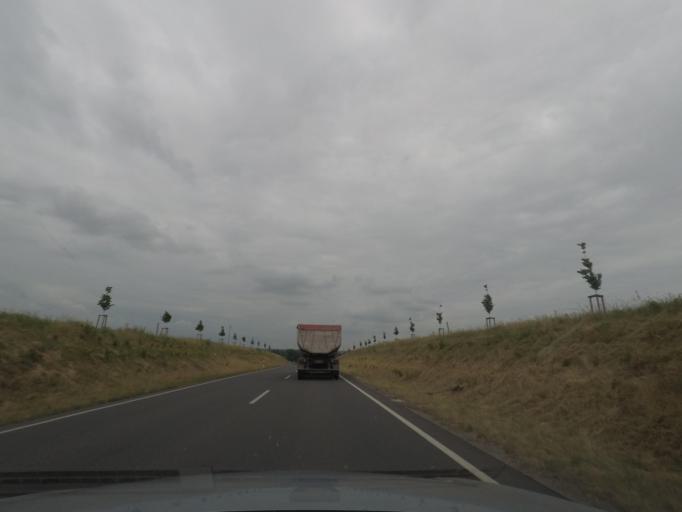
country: DE
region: Saxony-Anhalt
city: Suplingen
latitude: 52.2404
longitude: 11.3181
